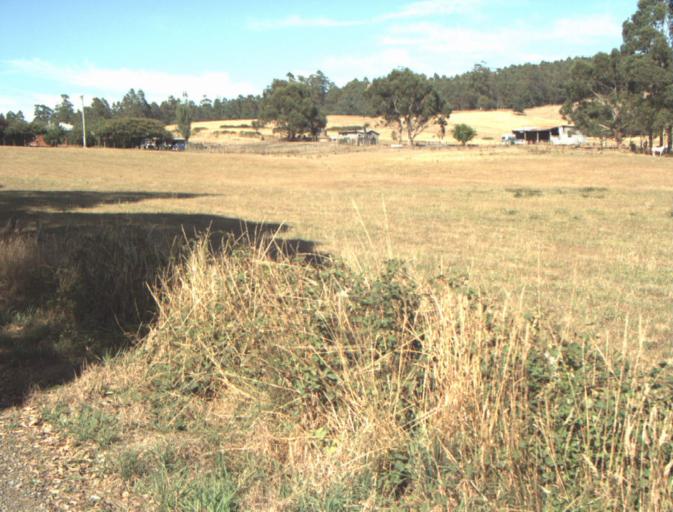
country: AU
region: Tasmania
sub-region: Launceston
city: Mayfield
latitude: -41.1764
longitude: 147.2158
